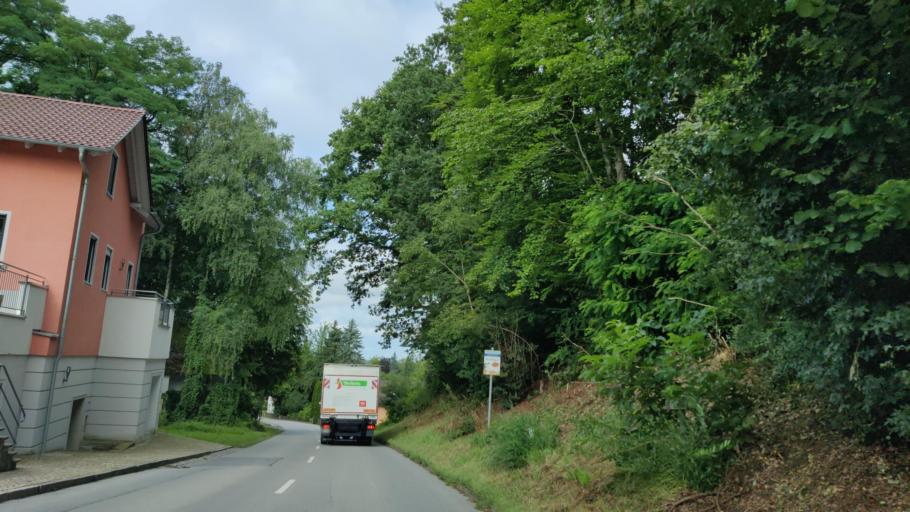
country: DE
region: Bavaria
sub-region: Lower Bavaria
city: Hofkirchen
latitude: 48.6790
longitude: 13.1250
